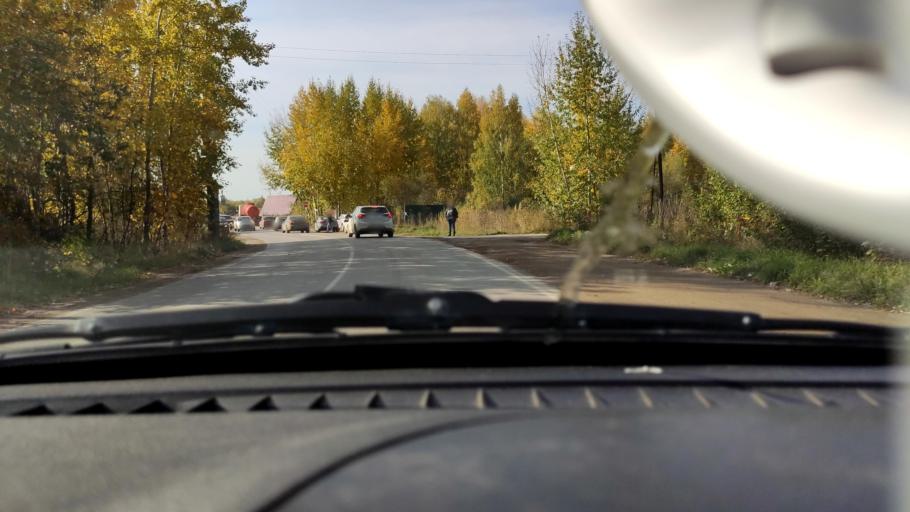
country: RU
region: Perm
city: Overyata
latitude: 58.0562
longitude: 55.8794
